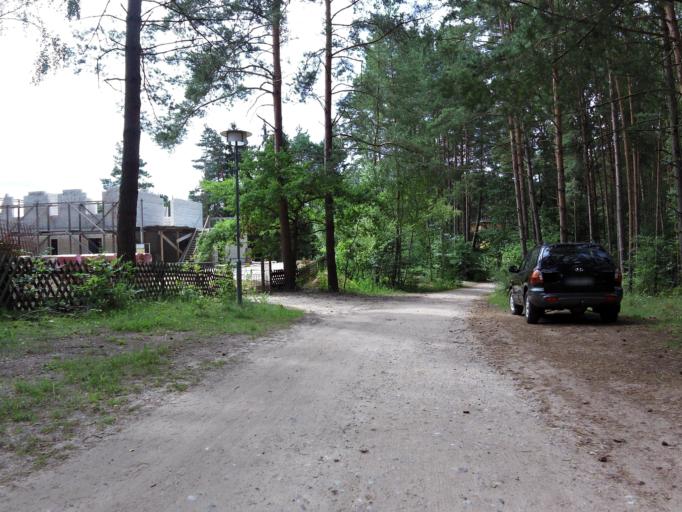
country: DE
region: Brandenburg
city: Lychen
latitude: 53.2214
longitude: 13.2783
